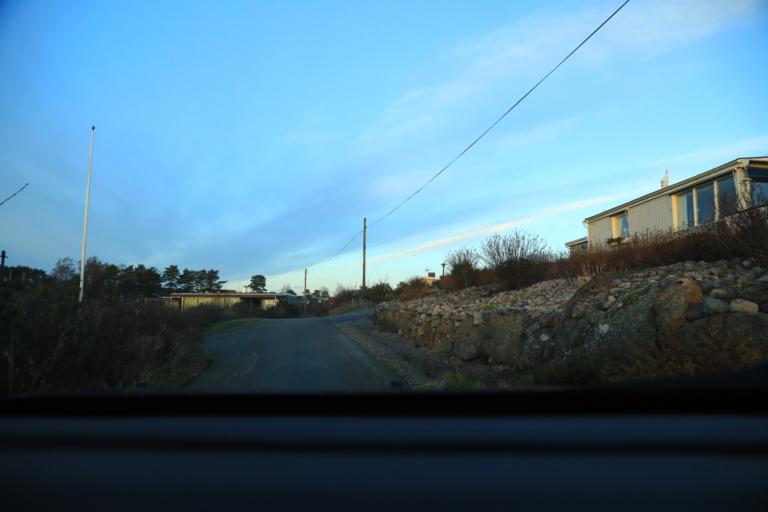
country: SE
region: Halland
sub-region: Varbergs Kommun
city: Varberg
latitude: 57.1874
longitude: 12.1737
